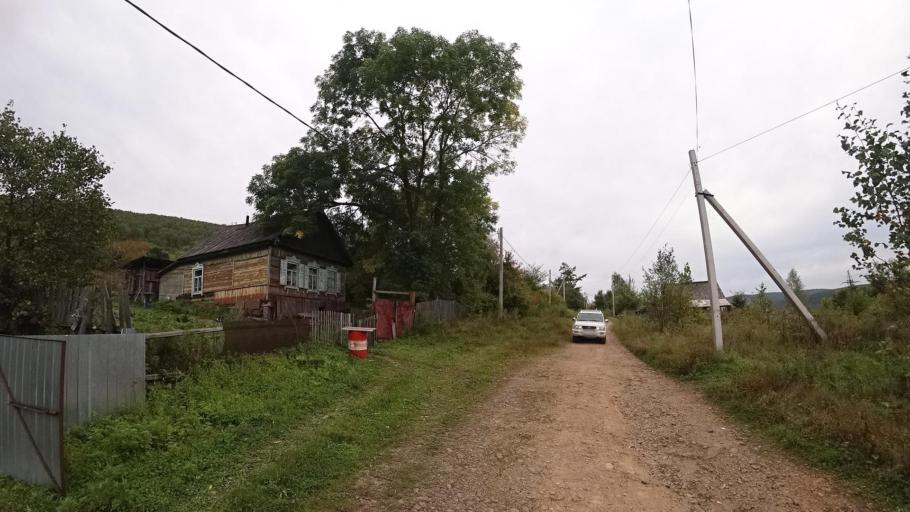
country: RU
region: Jewish Autonomous Oblast
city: Khingansk
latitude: 49.0377
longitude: 131.0607
